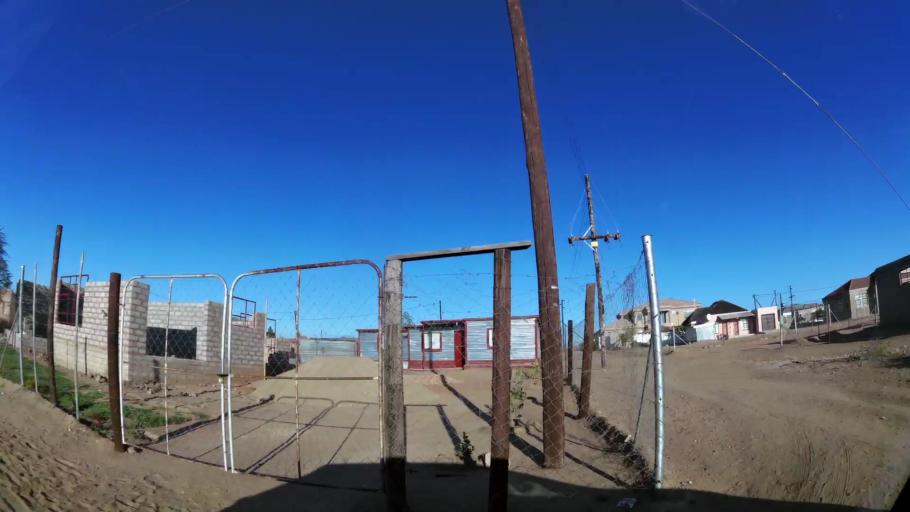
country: ZA
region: Limpopo
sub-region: Capricorn District Municipality
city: Polokwane
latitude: -23.8373
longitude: 29.3630
